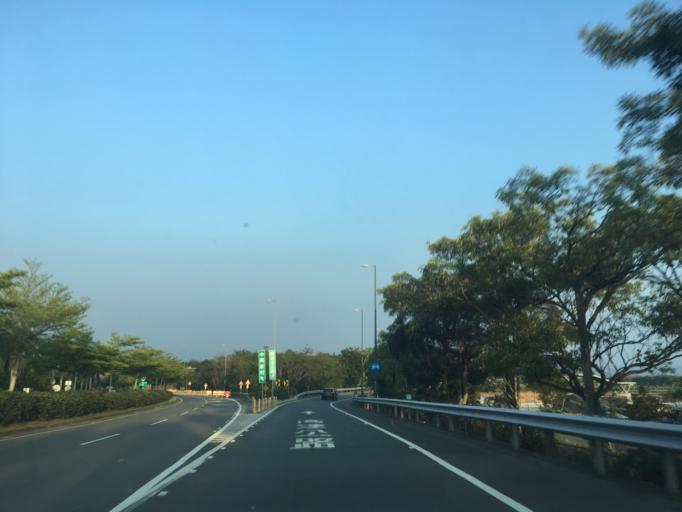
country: TW
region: Taiwan
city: Zhongxing New Village
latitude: 23.9492
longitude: 120.6660
